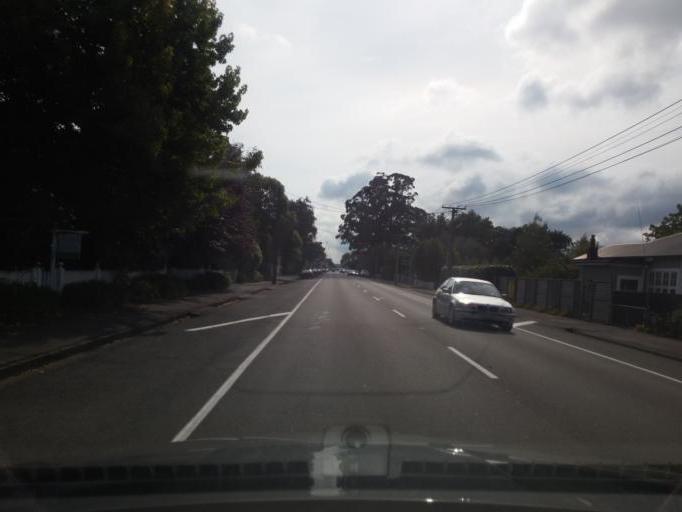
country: NZ
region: Wellington
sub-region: Masterton District
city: Masterton
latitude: -41.0839
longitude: 175.4563
